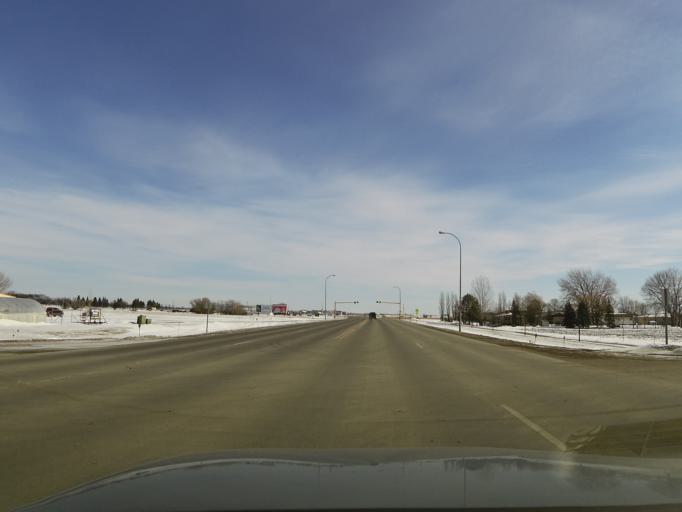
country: US
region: North Dakota
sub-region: Walsh County
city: Grafton
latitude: 48.4124
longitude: -97.3998
